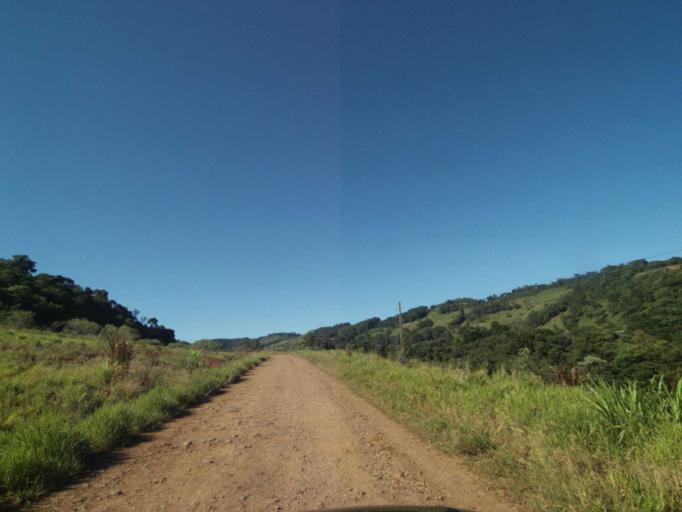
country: BR
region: Parana
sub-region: Francisco Beltrao
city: Francisco Beltrao
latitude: -26.1469
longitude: -53.3126
